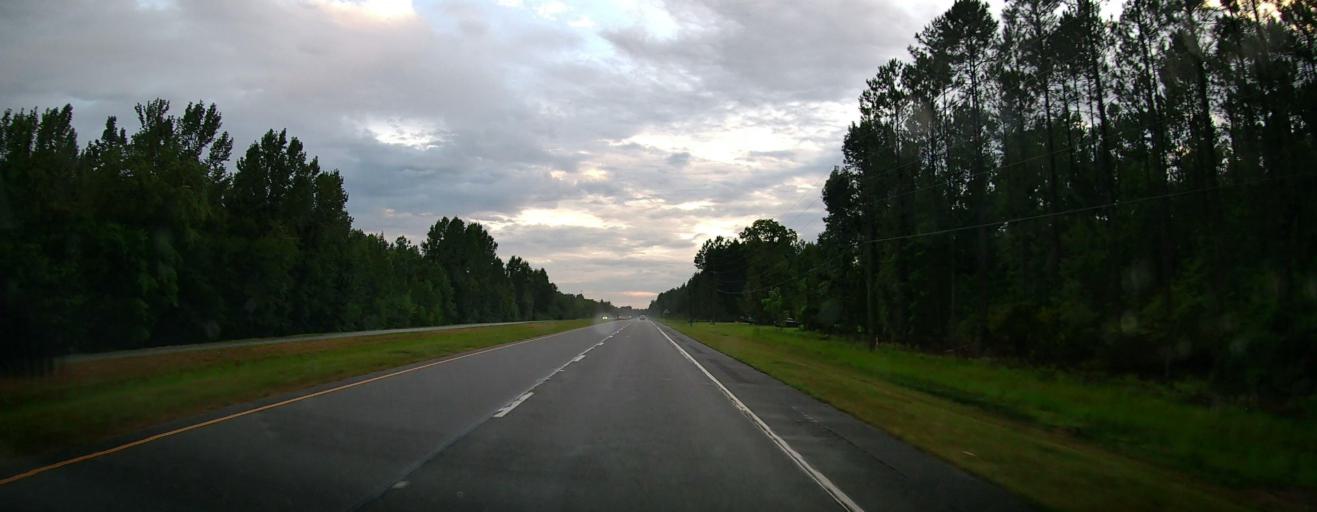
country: US
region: Georgia
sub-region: Lanier County
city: Lakeland
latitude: 30.9481
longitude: -82.9764
